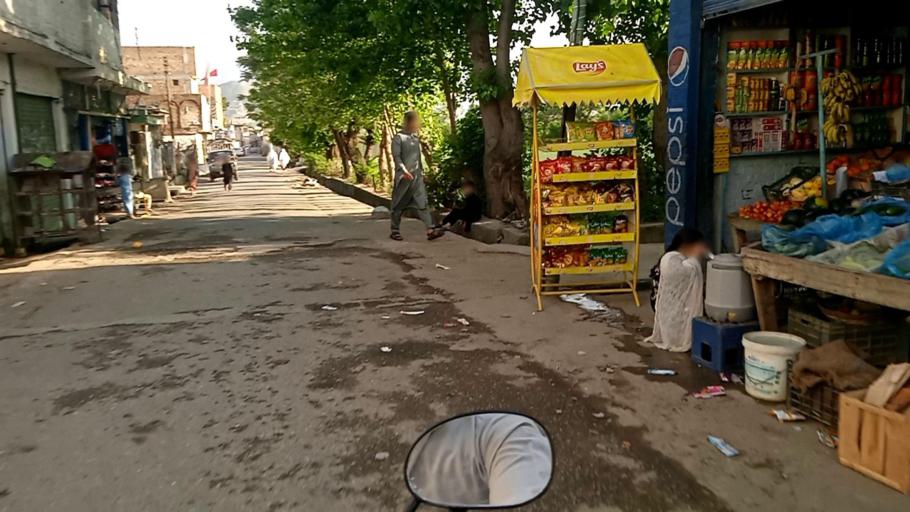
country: PK
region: Khyber Pakhtunkhwa
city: Mingora
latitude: 34.8114
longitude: 72.3602
